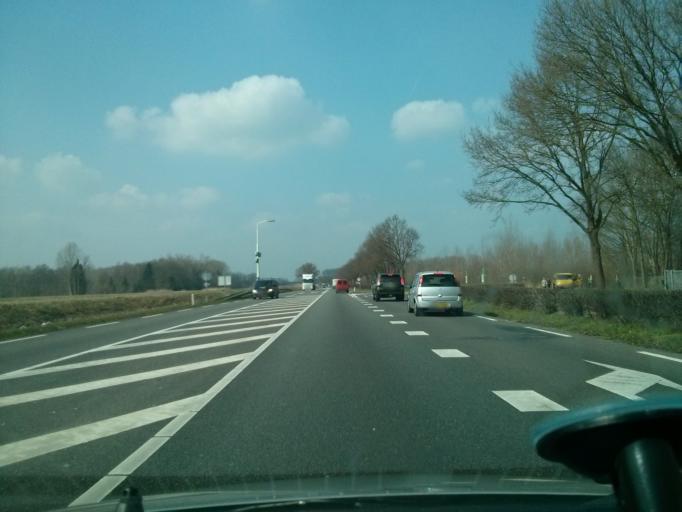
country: NL
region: North Brabant
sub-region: Gemeente Veghel
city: Eerde
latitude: 51.6372
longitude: 5.4789
